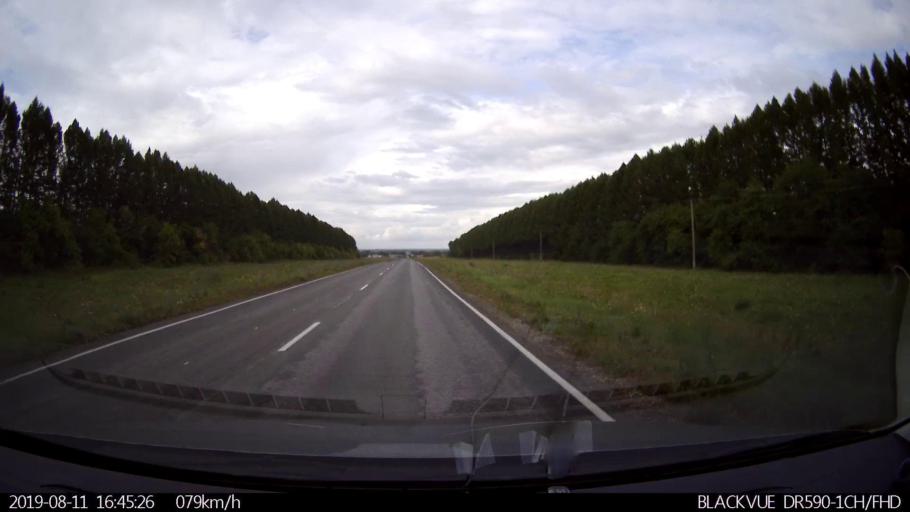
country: RU
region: Ulyanovsk
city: Mayna
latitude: 54.1897
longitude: 47.6860
